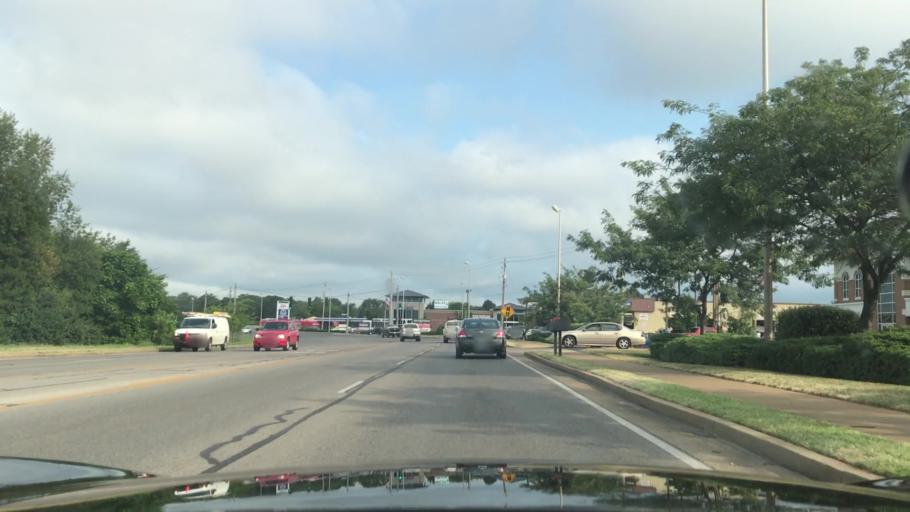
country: US
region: Kentucky
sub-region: Warren County
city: Bowling Green
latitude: 36.9593
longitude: -86.4501
